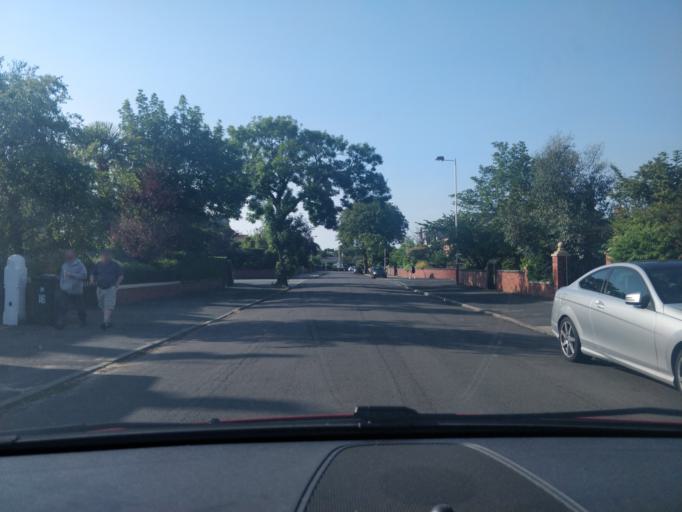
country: GB
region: England
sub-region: Sefton
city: Southport
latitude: 53.6515
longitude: -2.9741
